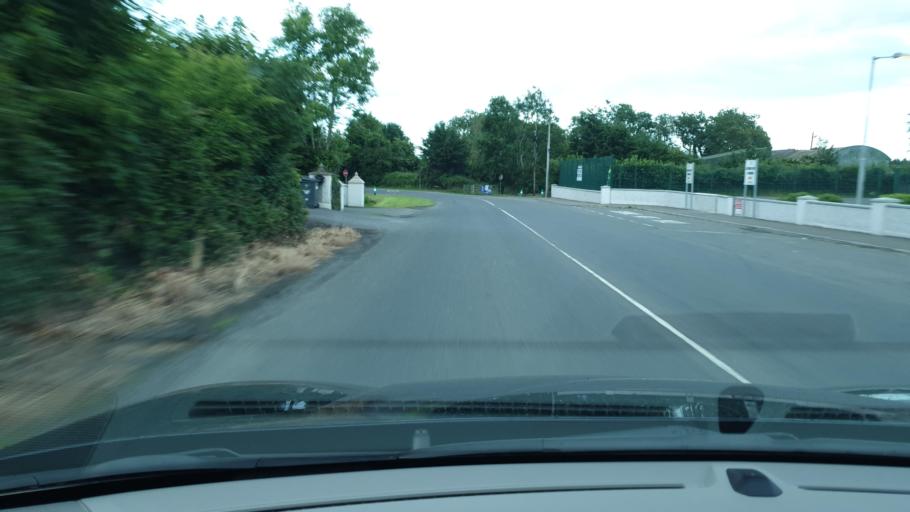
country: IE
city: Kentstown
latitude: 53.5902
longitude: -6.5021
